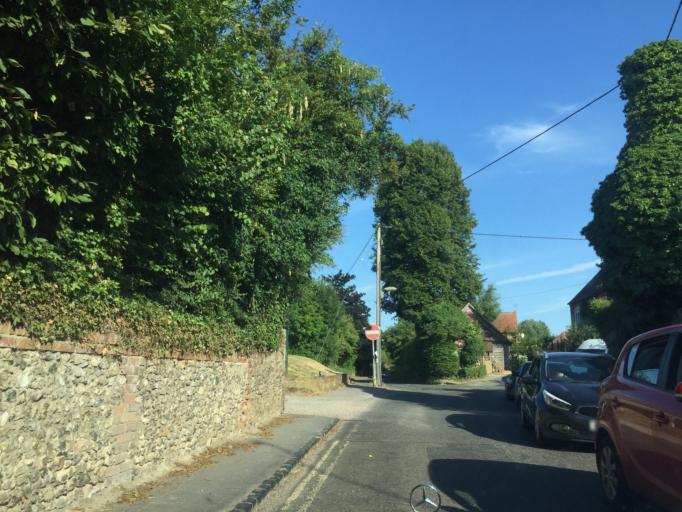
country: GB
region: England
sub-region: Oxfordshire
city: Watlington
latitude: 51.6431
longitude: -1.0059
